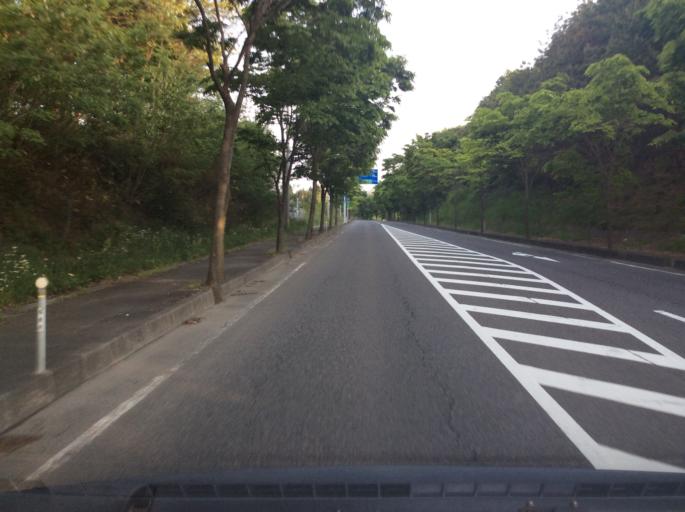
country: JP
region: Fukushima
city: Ishikawa
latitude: 37.2238
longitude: 140.4355
